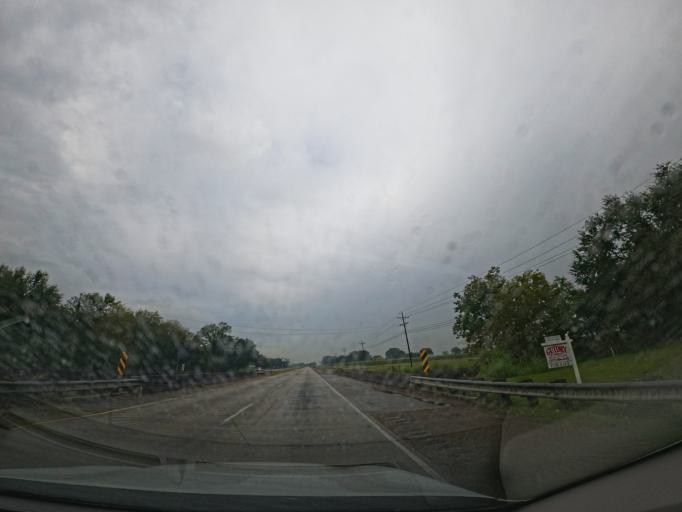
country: US
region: Louisiana
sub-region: Iberia Parish
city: Delcambre
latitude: 29.9642
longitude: -91.9247
